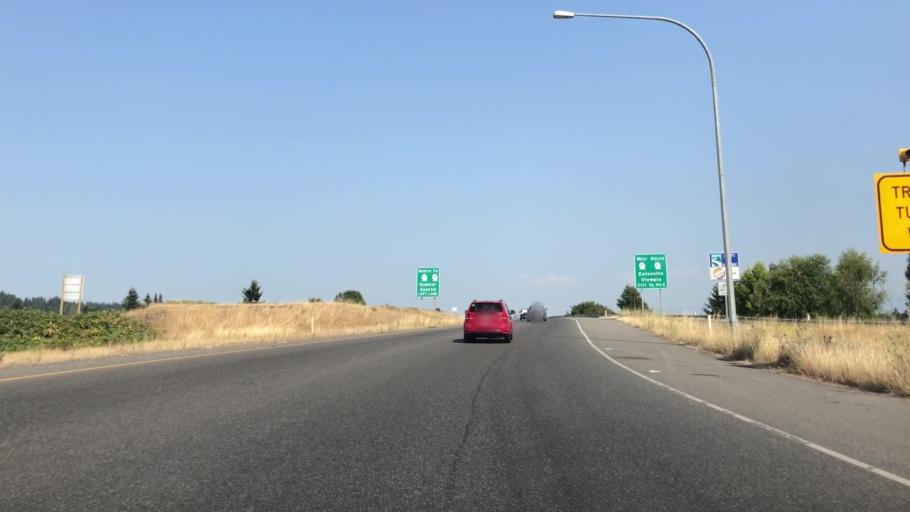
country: US
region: Washington
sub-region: Pierce County
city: North Puyallup
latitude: 47.2041
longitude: -122.2921
